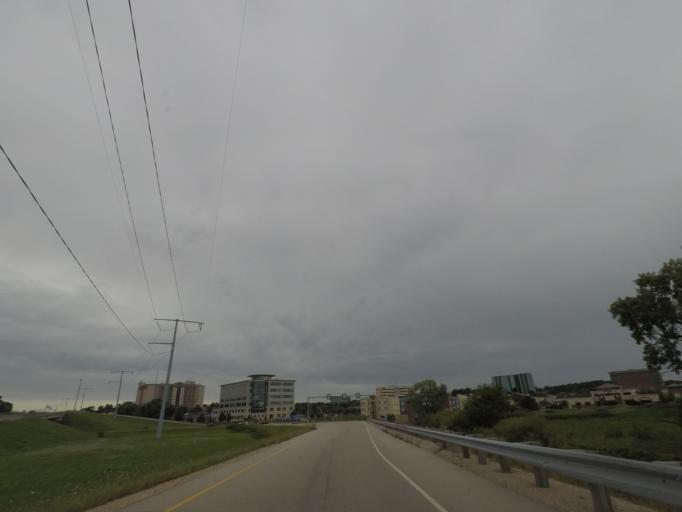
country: US
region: Wisconsin
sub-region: Dane County
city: Middleton
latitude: 43.0916
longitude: -89.5209
